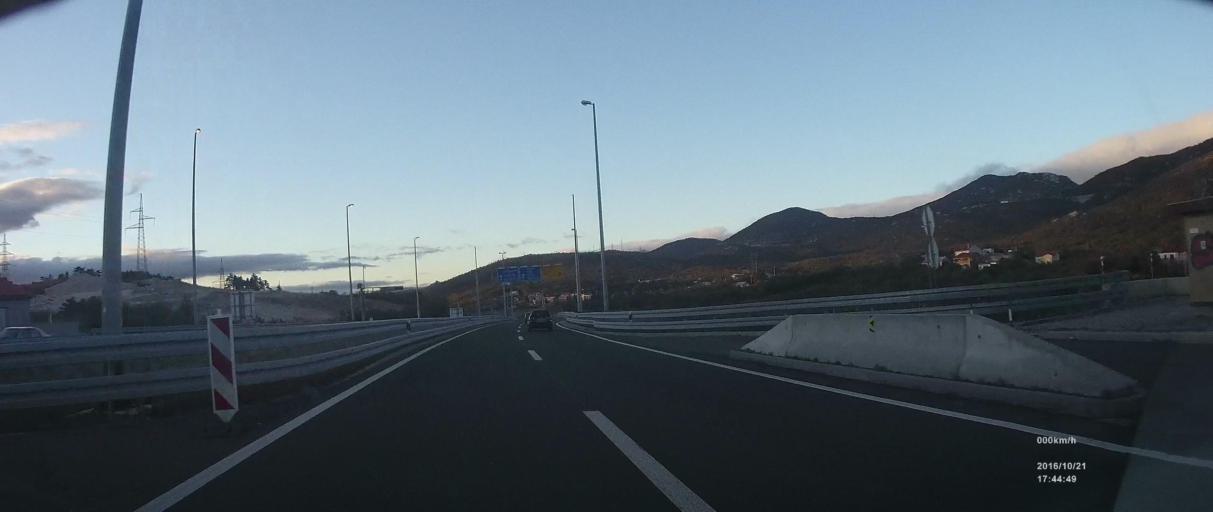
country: HR
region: Primorsko-Goranska
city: Hreljin
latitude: 45.2846
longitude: 14.5884
